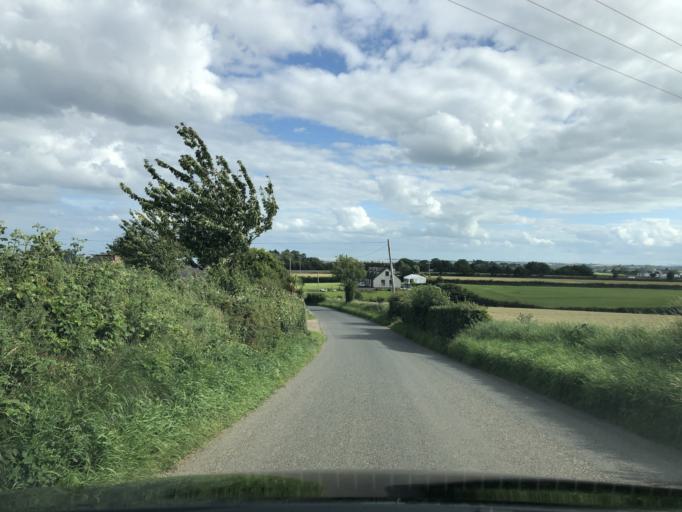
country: GB
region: Northern Ireland
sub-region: Ards District
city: Newtownards
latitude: 54.5623
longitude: -5.7100
